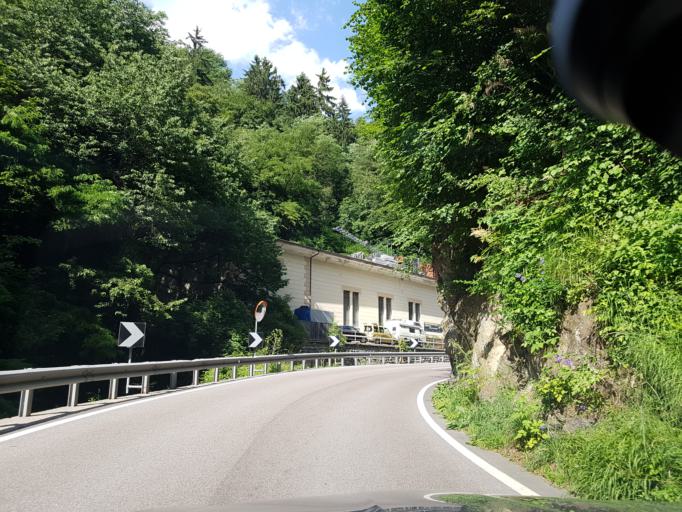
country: IT
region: Trentino-Alto Adige
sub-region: Bolzano
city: Ponte Gardena
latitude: 46.5988
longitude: 11.5424
